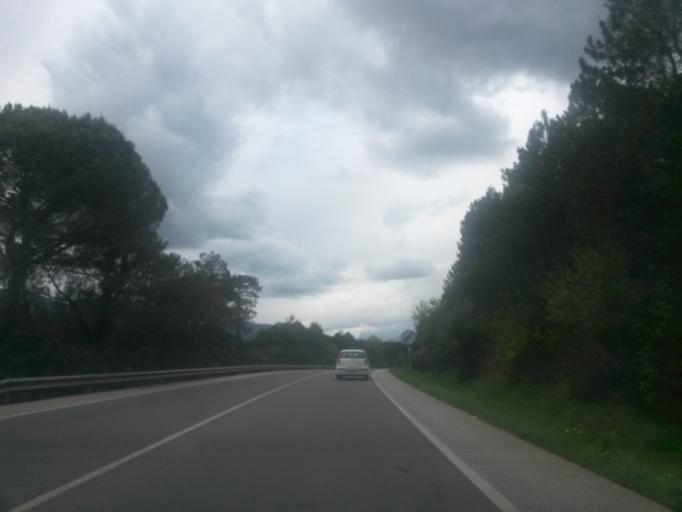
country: ES
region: Catalonia
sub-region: Provincia de Girona
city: Angles
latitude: 41.9334
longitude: 2.6446
